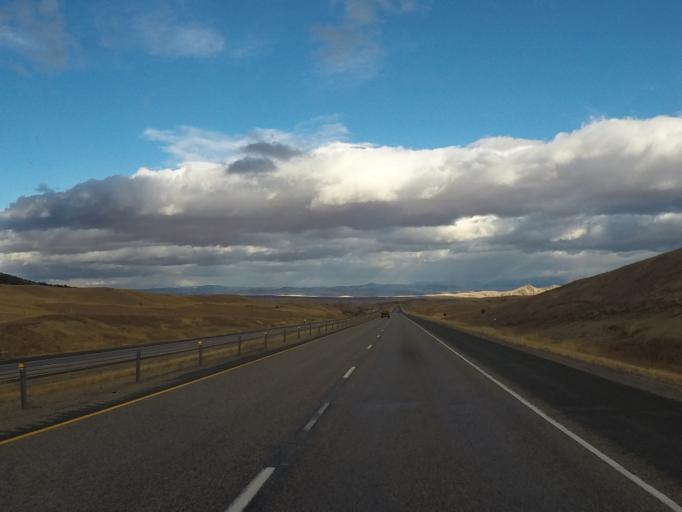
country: US
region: Montana
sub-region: Jefferson County
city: Whitehall
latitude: 45.8936
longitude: -111.8468
